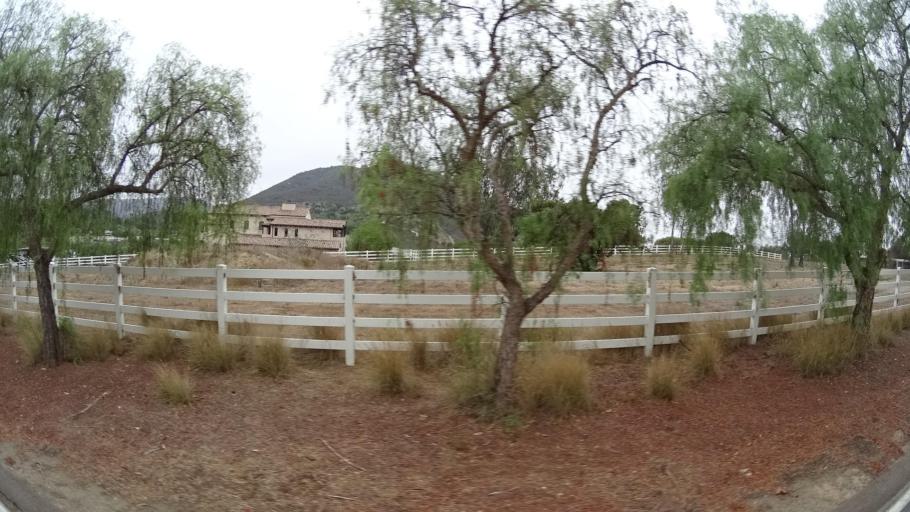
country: US
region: California
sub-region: San Diego County
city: Lake San Marcos
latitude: 33.0789
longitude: -117.1763
